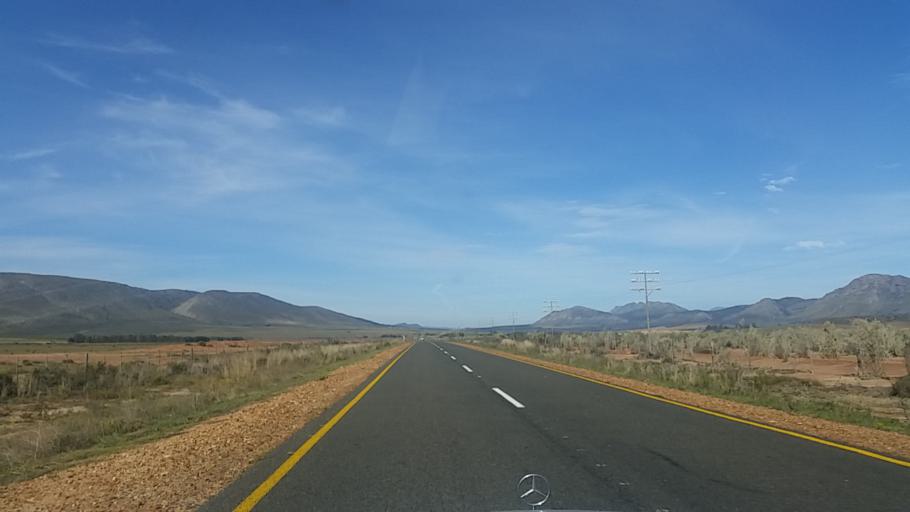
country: ZA
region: Western Cape
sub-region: Eden District Municipality
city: George
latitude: -33.8116
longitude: 22.5361
